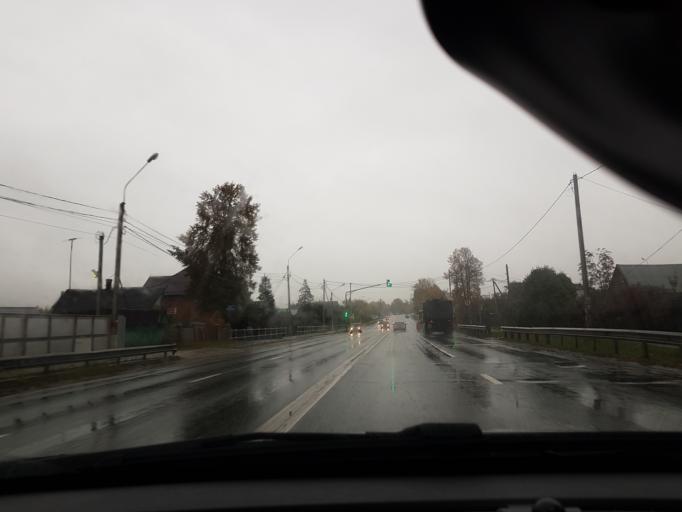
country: RU
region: Moskovskaya
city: Istra
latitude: 55.9082
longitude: 36.8799
